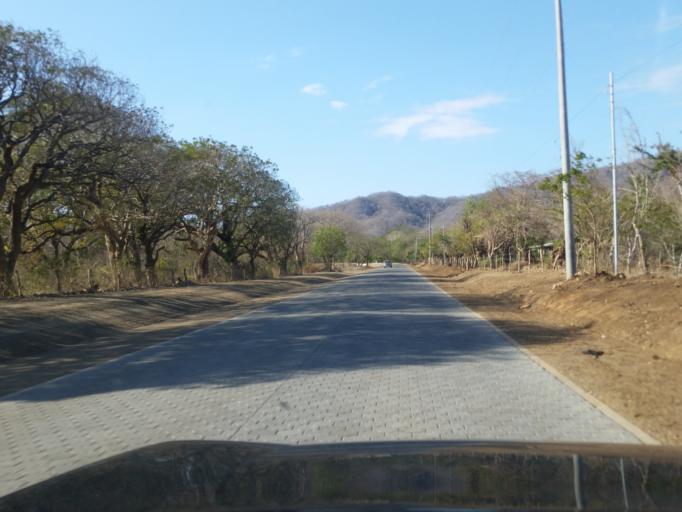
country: NI
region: Rivas
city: Tola
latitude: 11.4182
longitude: -86.0091
